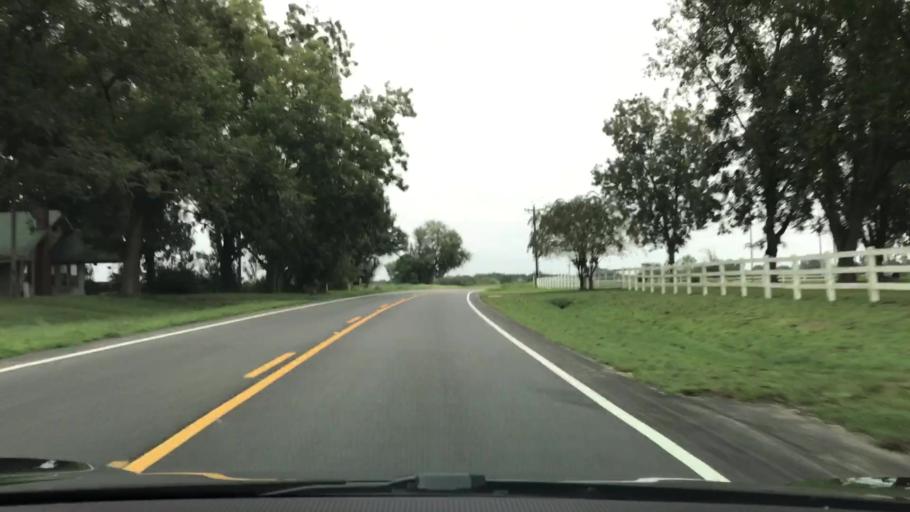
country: US
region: Alabama
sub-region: Covington County
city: Opp
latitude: 31.2354
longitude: -86.1621
